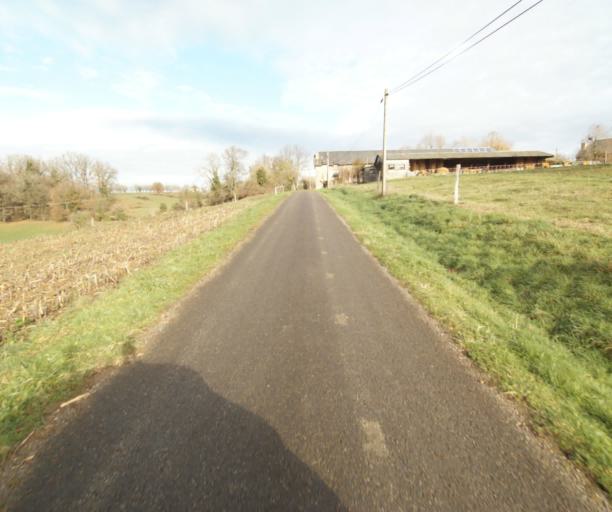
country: FR
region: Limousin
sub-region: Departement de la Correze
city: Saint-Mexant
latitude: 45.2790
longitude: 1.5978
